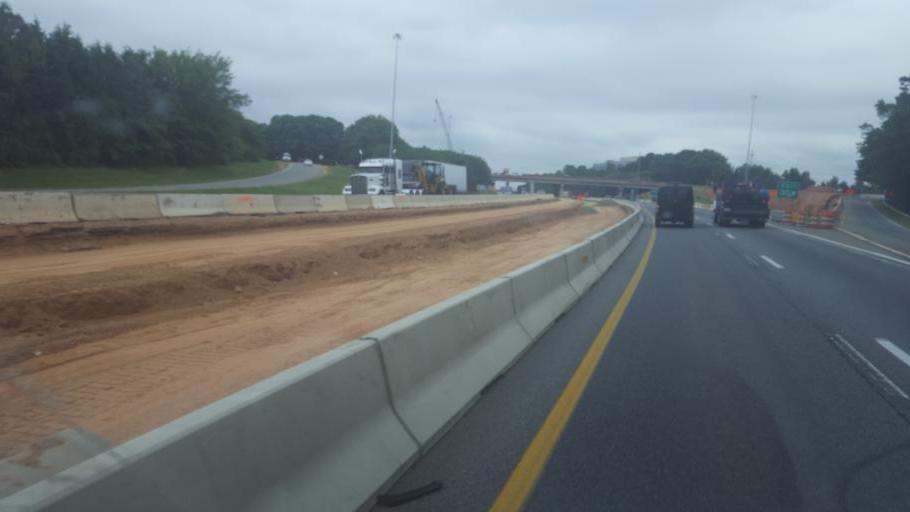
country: US
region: North Carolina
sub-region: Mecklenburg County
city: Cornelius
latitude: 35.5016
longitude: -80.8670
